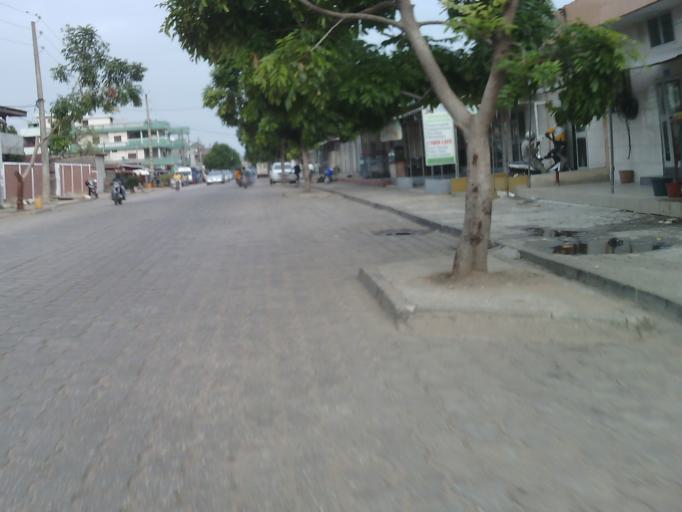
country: BJ
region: Littoral
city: Cotonou
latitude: 6.3887
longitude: 2.3780
